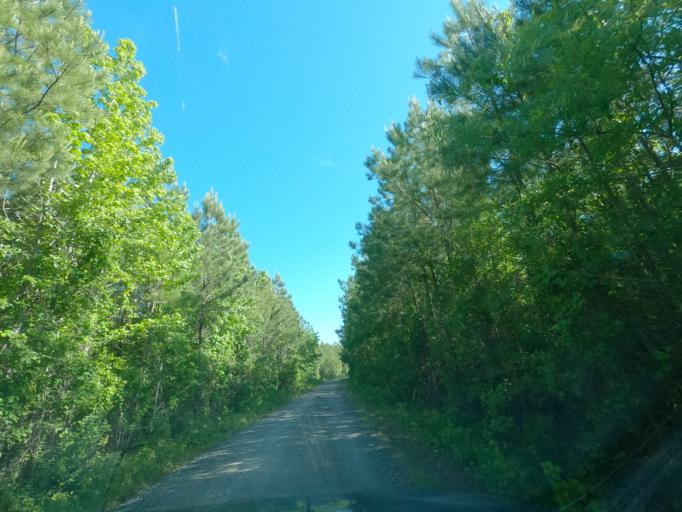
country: US
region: Georgia
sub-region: Columbia County
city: Evans
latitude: 33.6071
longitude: -82.1136
